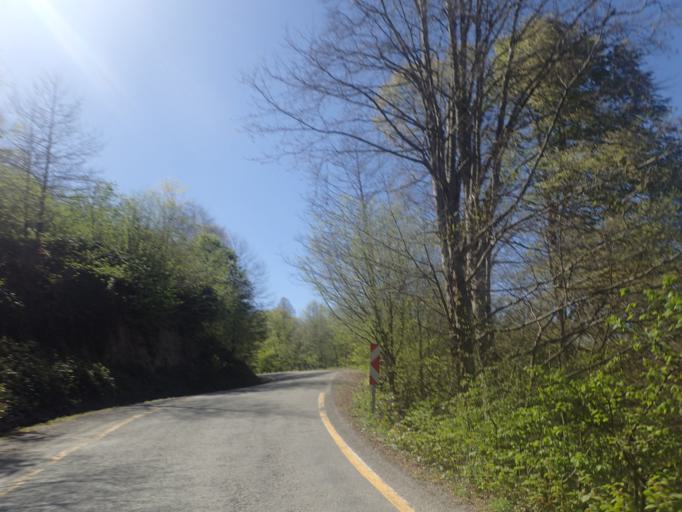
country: TR
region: Ordu
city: Kabaduz
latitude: 40.8136
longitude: 37.9070
